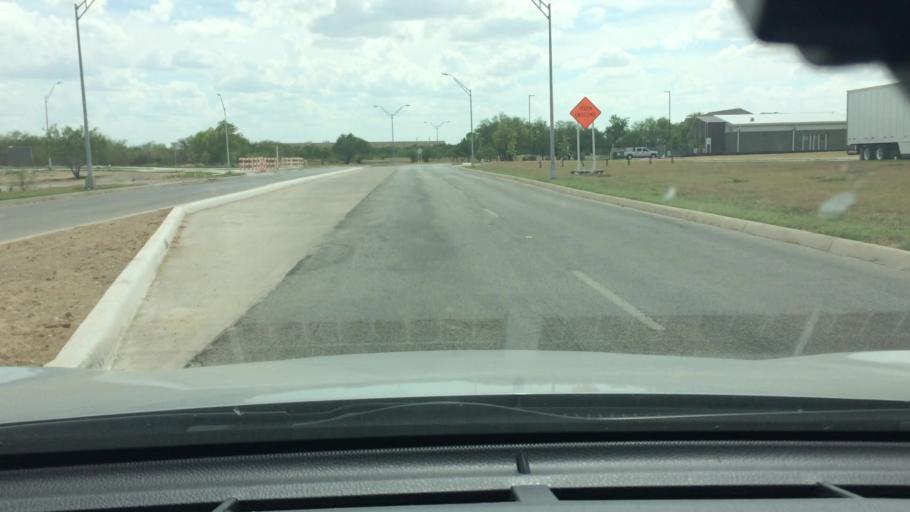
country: US
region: Texas
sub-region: Bexar County
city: China Grove
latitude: 29.3456
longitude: -98.4293
